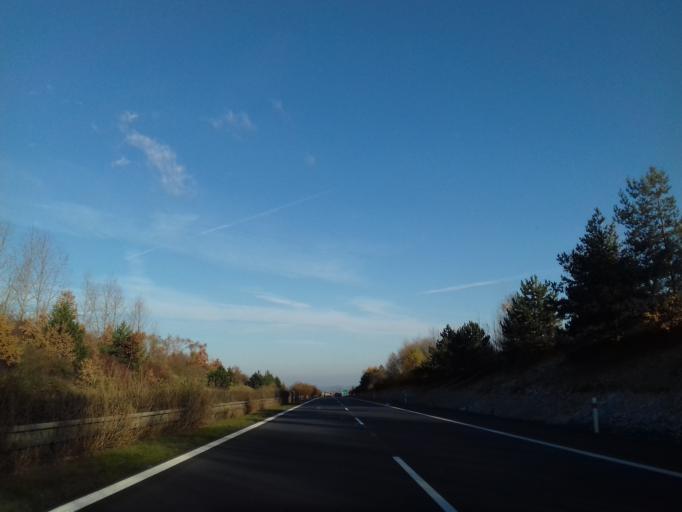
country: CZ
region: Plzensky
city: Zbiroh
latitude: 49.8378
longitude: 13.7977
